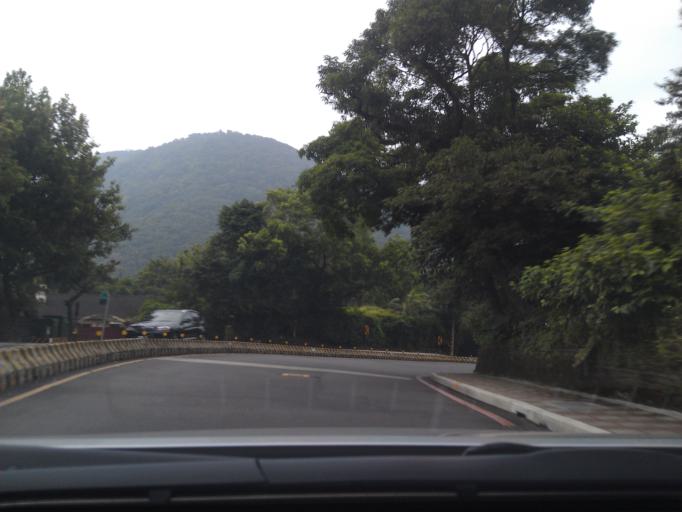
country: TW
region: Taipei
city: Taipei
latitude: 25.1395
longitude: 121.5464
